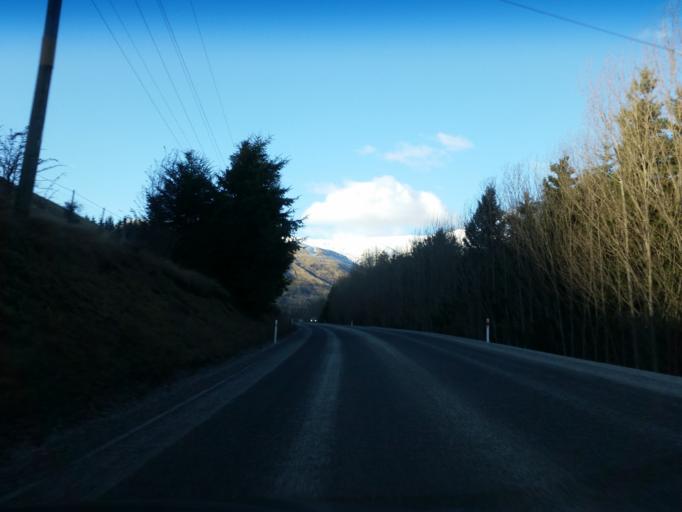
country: NZ
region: Otago
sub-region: Queenstown-Lakes District
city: Arrowtown
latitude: -44.9458
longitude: 168.7962
